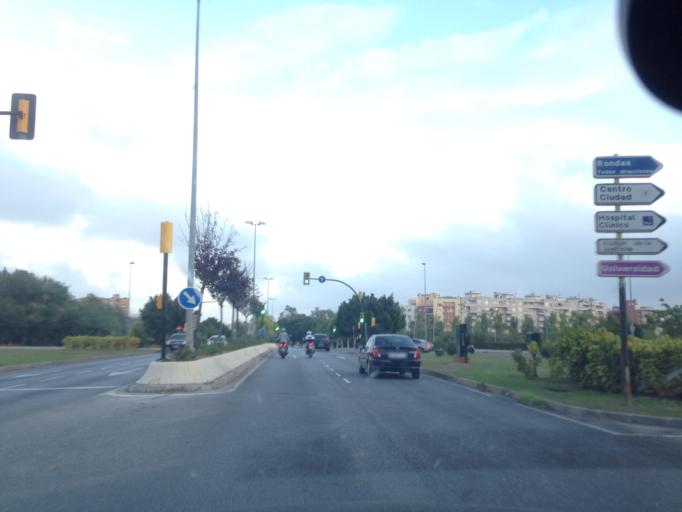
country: ES
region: Andalusia
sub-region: Provincia de Malaga
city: Malaga
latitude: 36.7275
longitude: -4.4637
